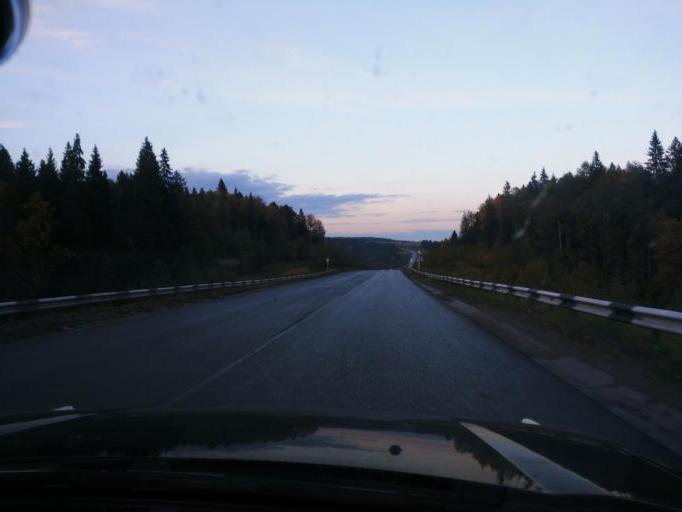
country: RU
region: Perm
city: Polazna
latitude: 58.2807
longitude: 56.4377
